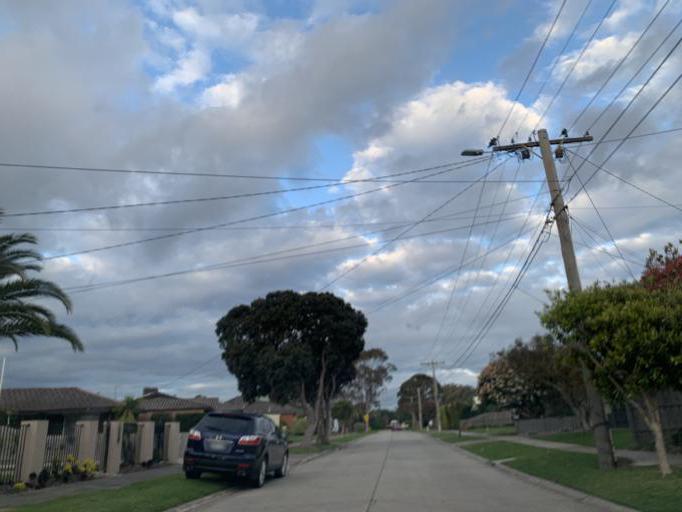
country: AU
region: Victoria
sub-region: Kingston
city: Aspendale
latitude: -38.0217
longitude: 145.1064
